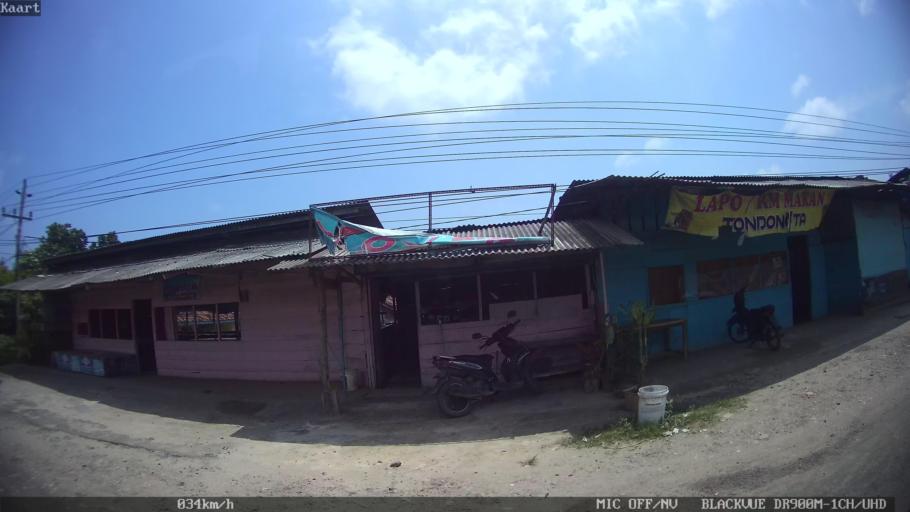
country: ID
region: Lampung
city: Kedaton
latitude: -5.3663
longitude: 105.2678
